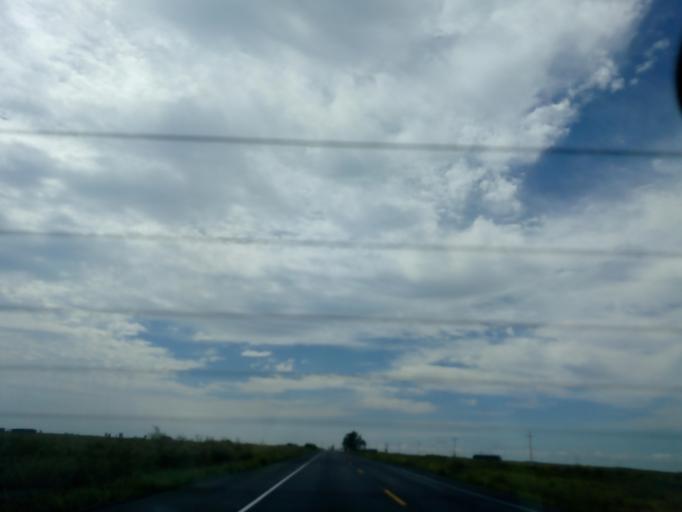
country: BR
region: Rio Grande do Sul
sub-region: Quarai
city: Quarai
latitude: -29.9772
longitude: -56.5489
